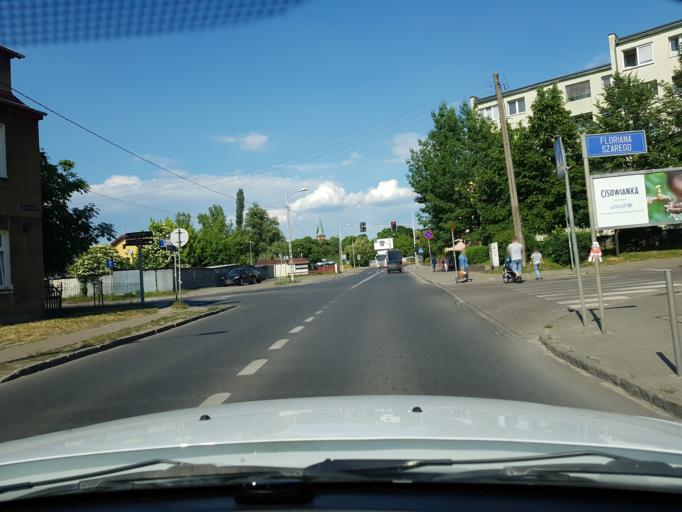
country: PL
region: West Pomeranian Voivodeship
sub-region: Szczecin
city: Szczecin
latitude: 53.3665
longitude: 14.5950
